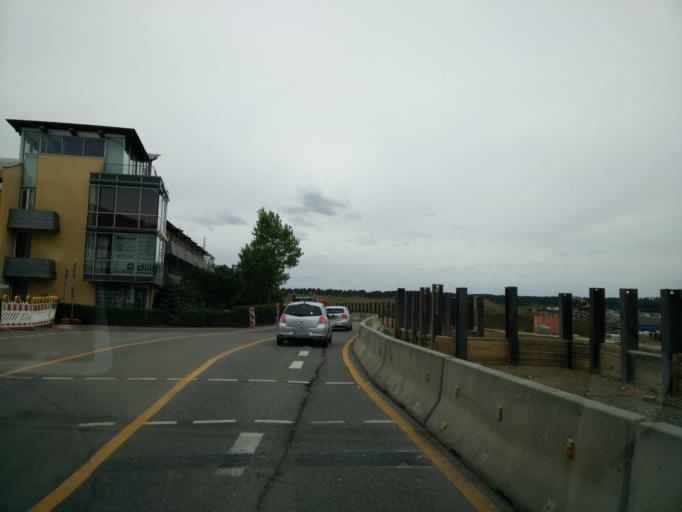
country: DE
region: Baden-Wuerttemberg
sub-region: Regierungsbezirk Stuttgart
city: Holzgerlingen
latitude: 48.6362
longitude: 9.0062
